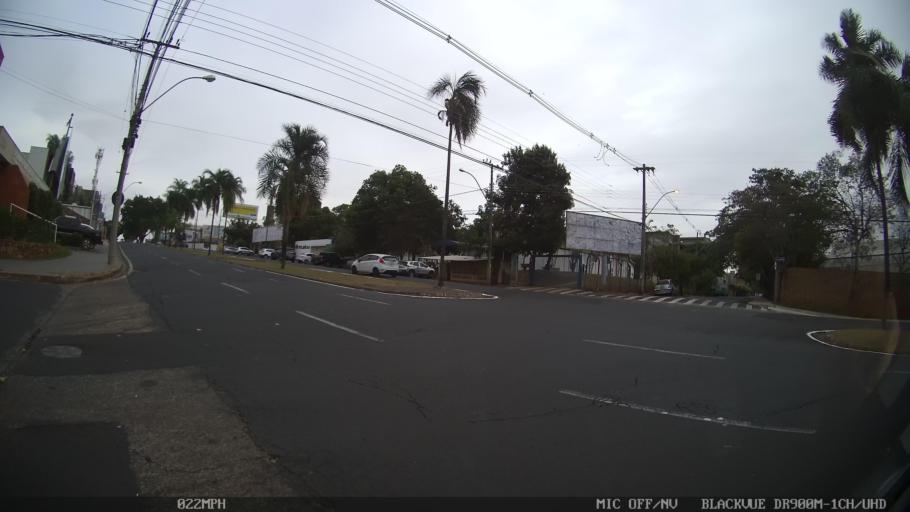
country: BR
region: Sao Paulo
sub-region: Sao Jose Do Rio Preto
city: Sao Jose do Rio Preto
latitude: -20.8341
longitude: -49.3946
